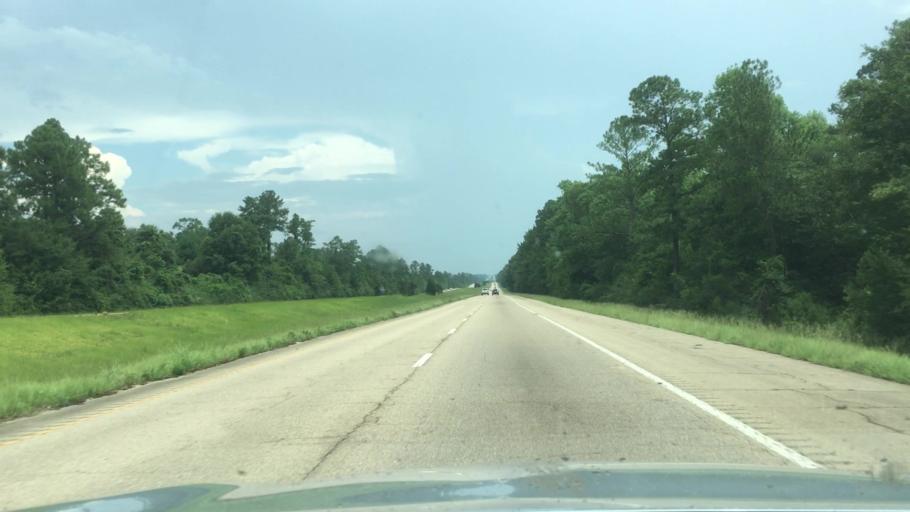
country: US
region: Mississippi
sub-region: Lamar County
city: Lumberton
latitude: 30.9593
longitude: -89.4396
